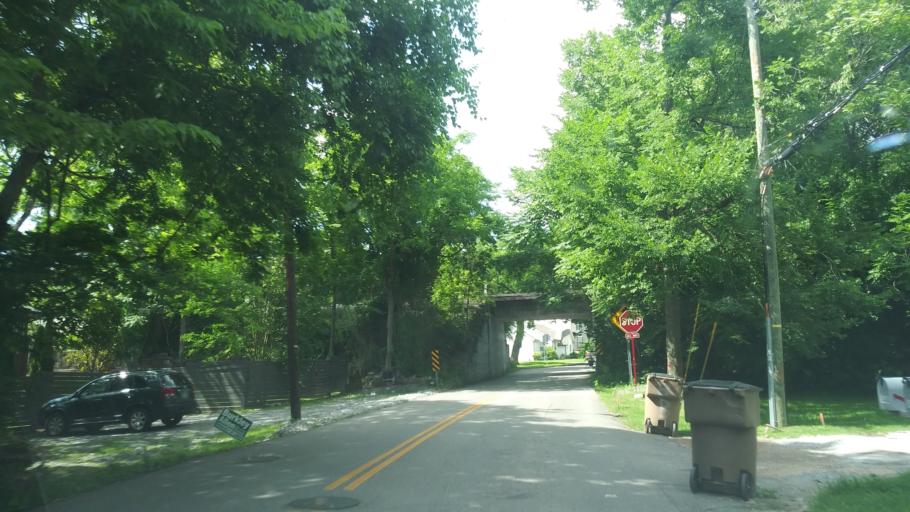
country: US
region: Tennessee
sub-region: Davidson County
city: Nashville
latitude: 36.1440
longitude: -86.8291
